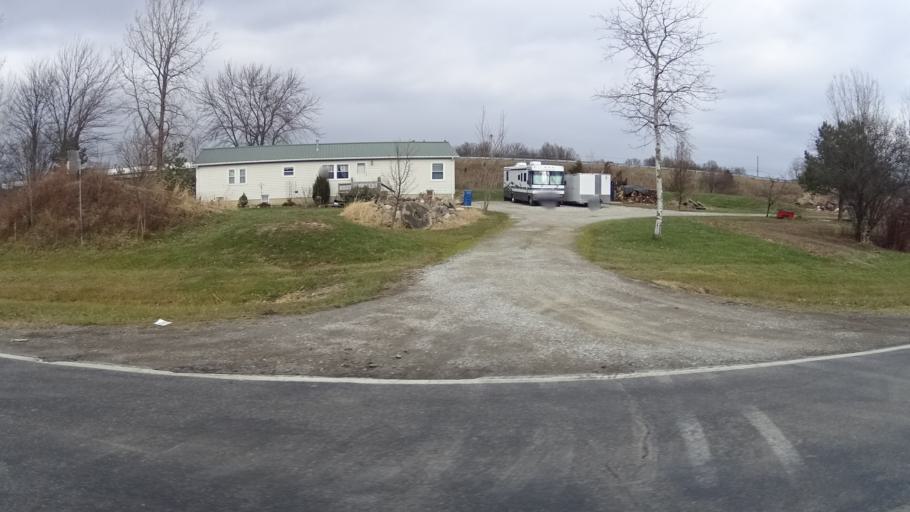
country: US
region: Ohio
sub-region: Lorain County
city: Oberlin
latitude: 41.2809
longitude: -82.1845
